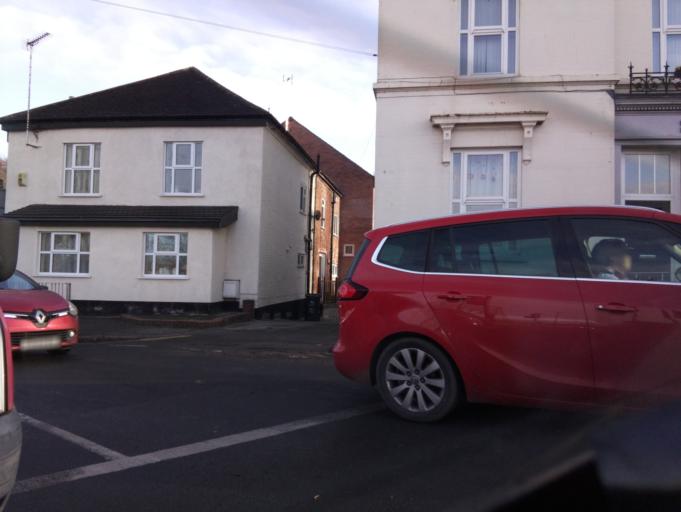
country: GB
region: England
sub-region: Staffordshire
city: Burton upon Trent
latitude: 52.8060
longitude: -1.6191
